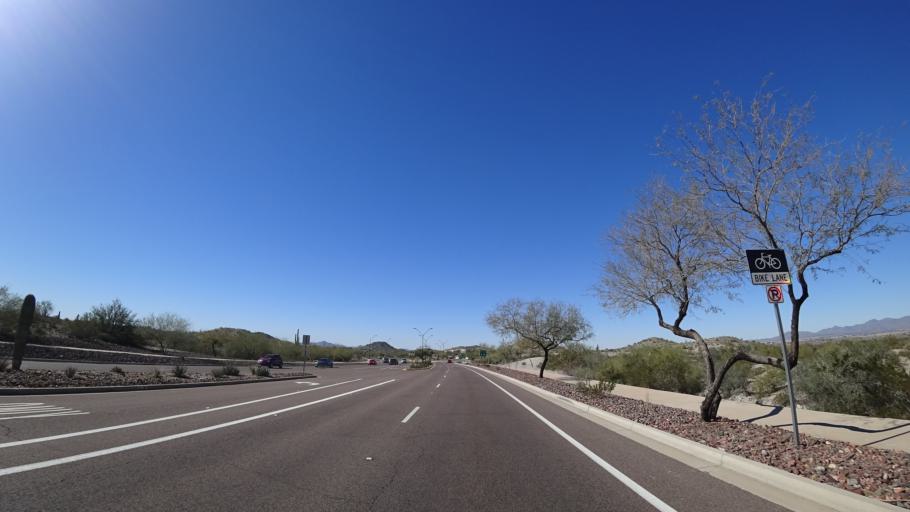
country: US
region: Arizona
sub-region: Maricopa County
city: Goodyear
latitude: 33.3584
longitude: -112.4196
